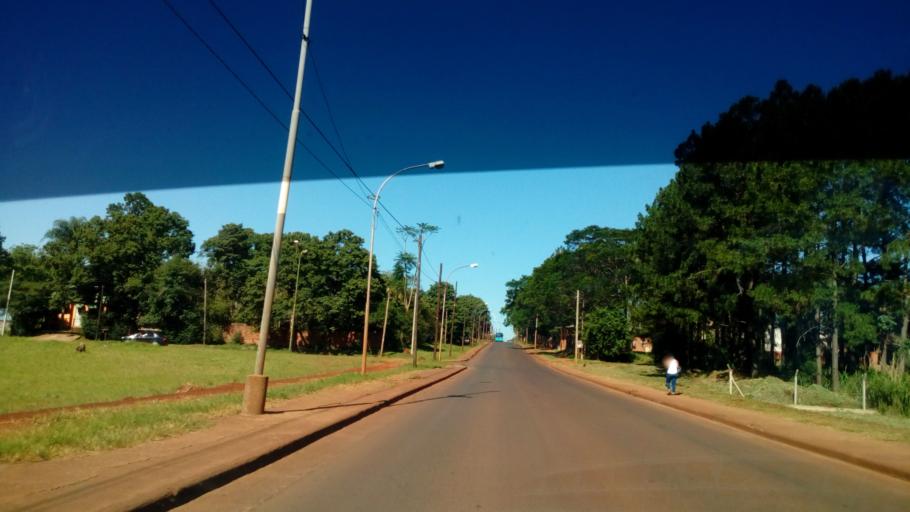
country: AR
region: Misiones
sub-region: Departamento de Capital
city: Posadas
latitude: -27.4281
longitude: -55.9018
